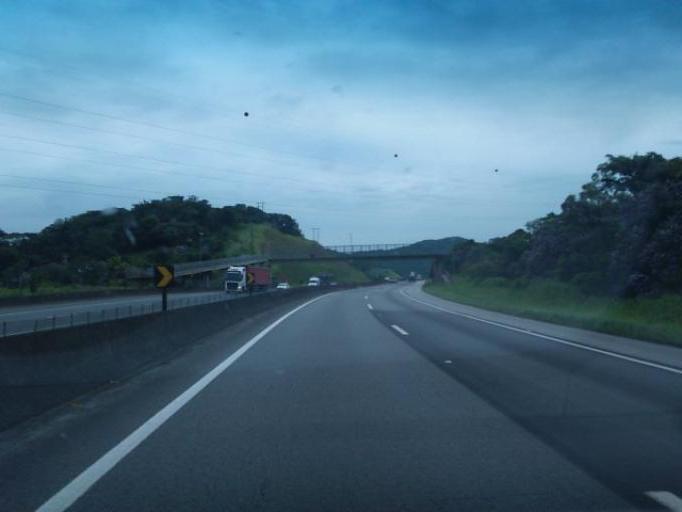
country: BR
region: Sao Paulo
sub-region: Juquia
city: Juquia
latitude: -24.3484
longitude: -47.6511
